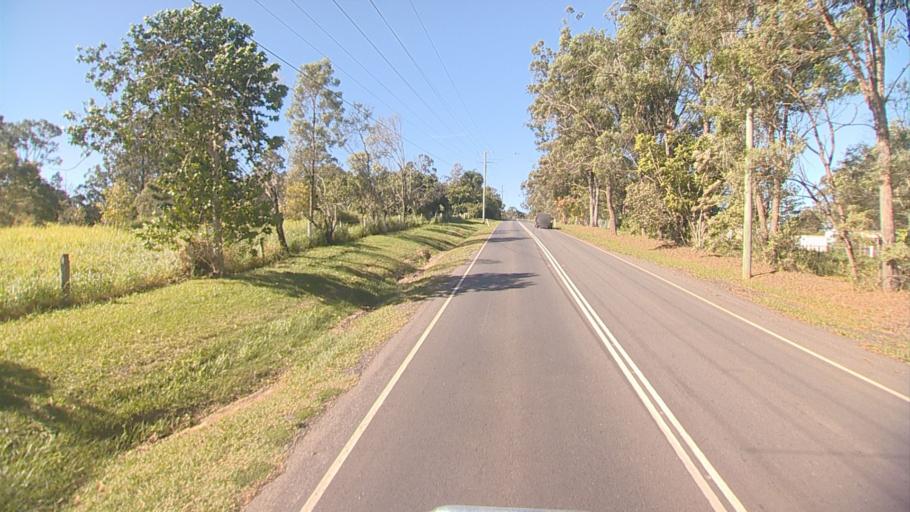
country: AU
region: Queensland
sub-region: Logan
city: Rochedale South
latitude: -27.5910
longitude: 153.1445
